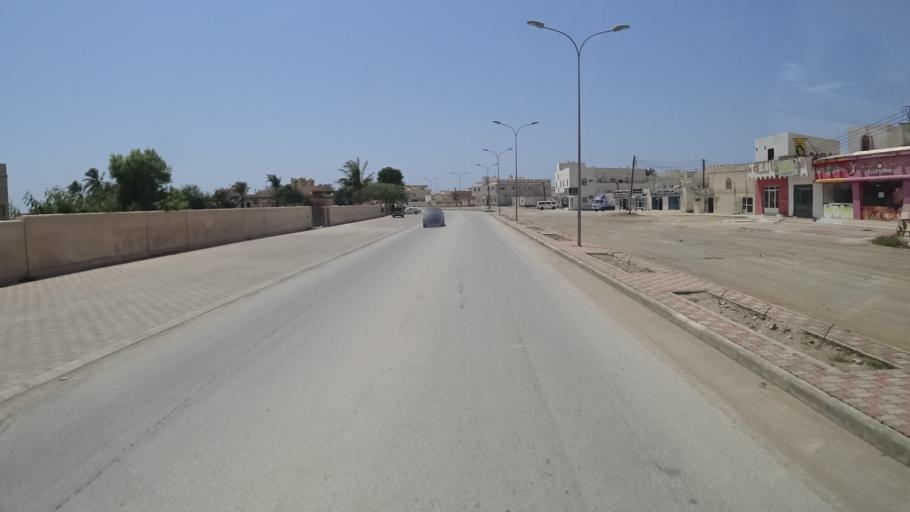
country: OM
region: Zufar
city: Salalah
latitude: 16.9860
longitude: 54.6948
